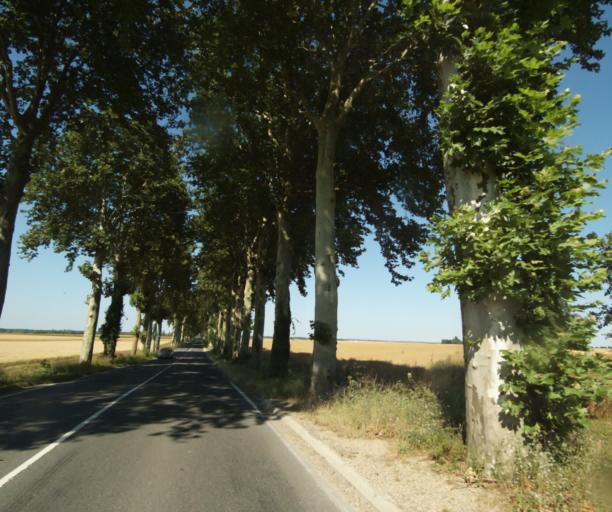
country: FR
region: Ile-de-France
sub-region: Departement de Seine-et-Marne
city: La Chapelle-la-Reine
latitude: 48.3264
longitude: 2.5837
